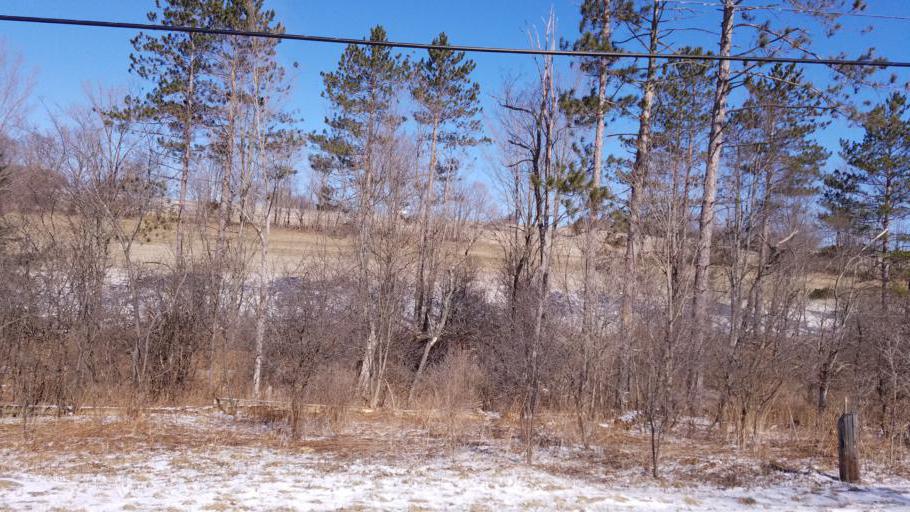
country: US
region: New York
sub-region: Allegany County
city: Andover
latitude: 42.0656
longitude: -77.8191
